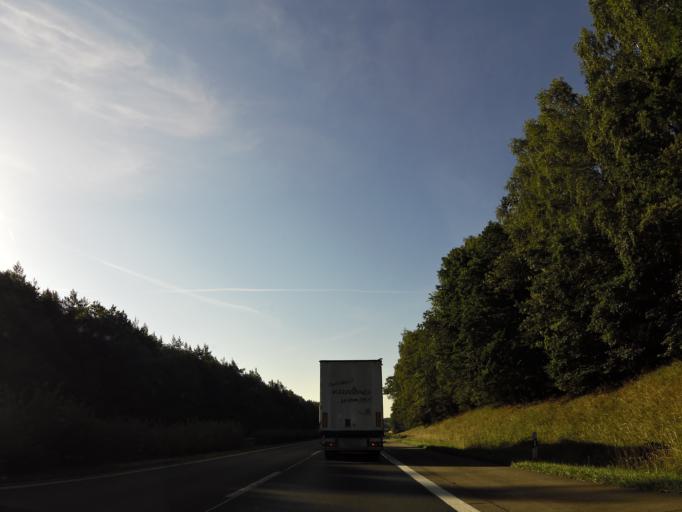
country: DE
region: Bavaria
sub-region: Regierungsbezirk Mittelfranken
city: Hochstadt an der Aisch
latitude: 49.7326
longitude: 10.8134
